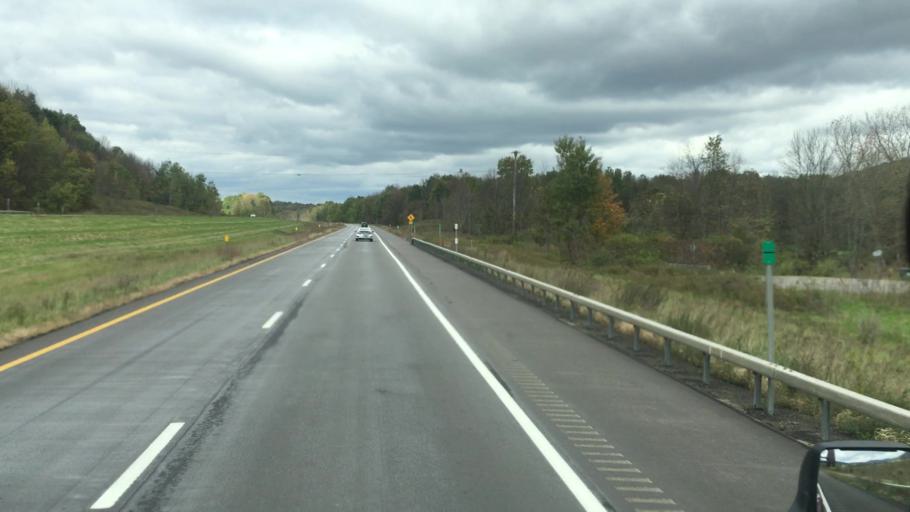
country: US
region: New York
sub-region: Cattaraugus County
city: Randolph
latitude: 42.1113
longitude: -78.9211
